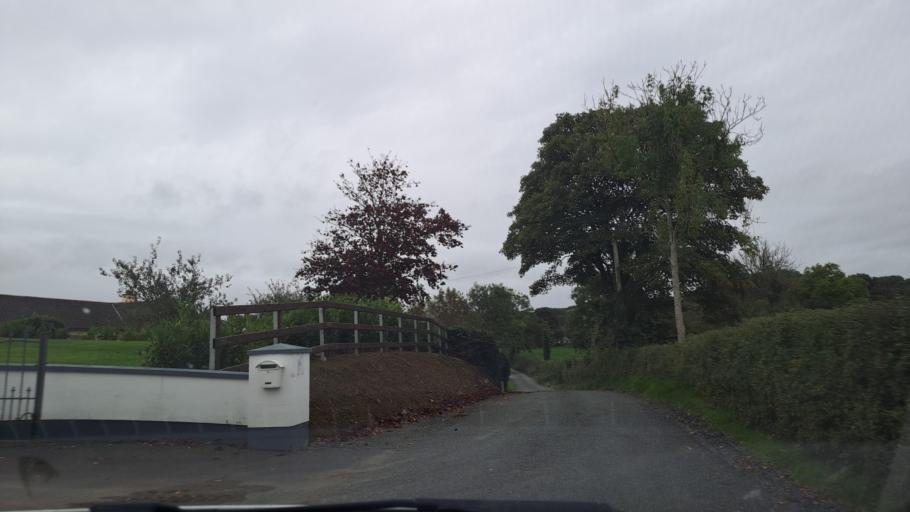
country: IE
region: Ulster
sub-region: County Monaghan
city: Carrickmacross
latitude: 53.9824
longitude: -6.7530
